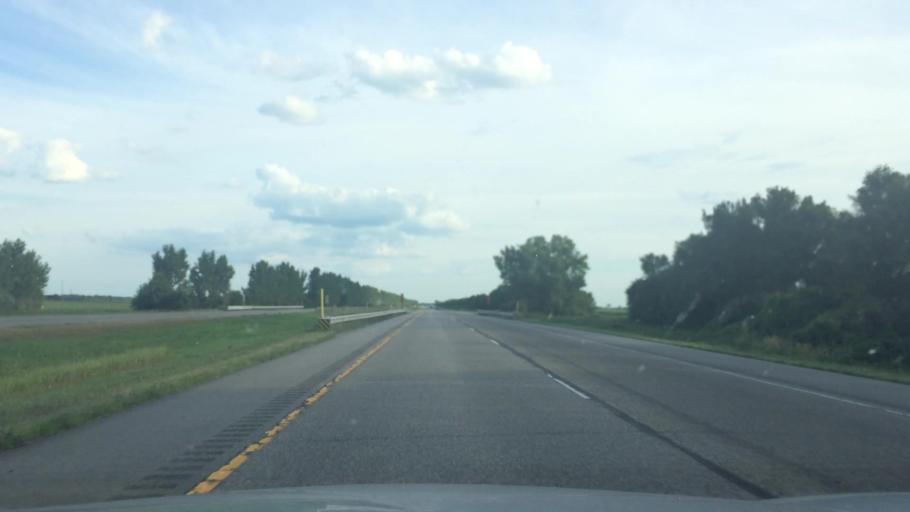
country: US
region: Wisconsin
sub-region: Portage County
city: Plover
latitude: 44.3612
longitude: -89.5208
